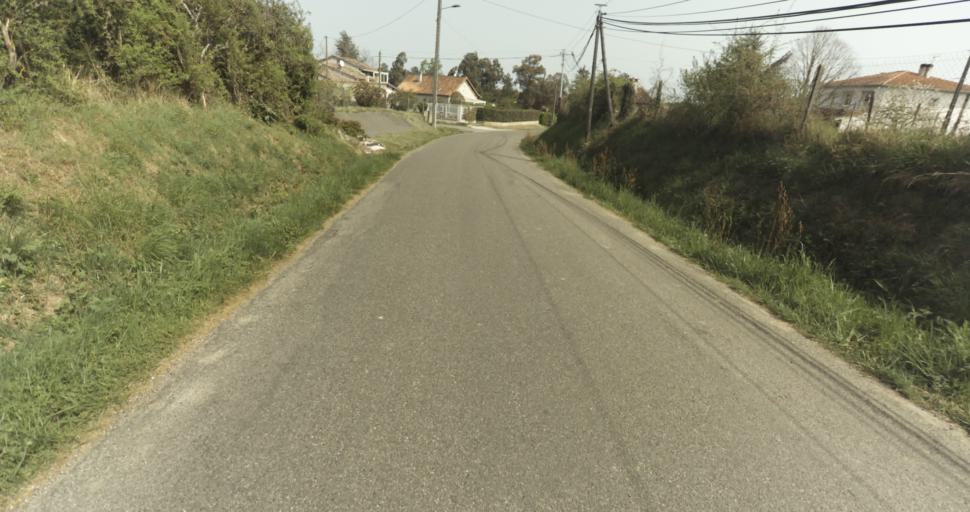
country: FR
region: Midi-Pyrenees
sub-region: Departement du Tarn-et-Garonne
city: Moissac
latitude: 44.1124
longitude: 1.0714
